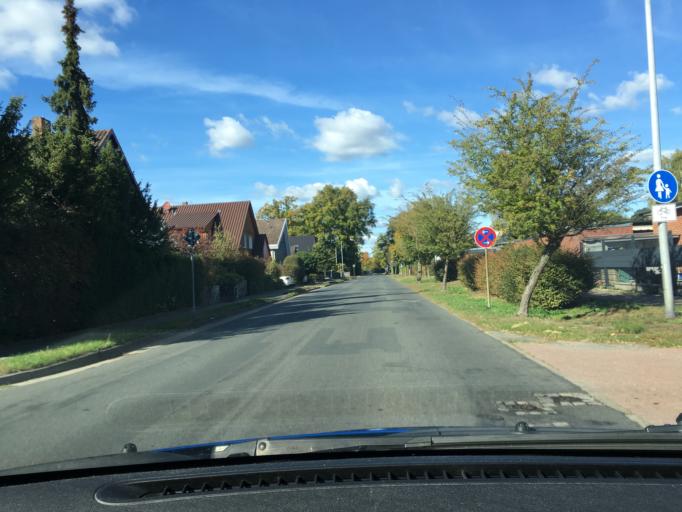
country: DE
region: Lower Saxony
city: Isernhagen Farster Bauerschaft
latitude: 52.4967
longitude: 9.8586
